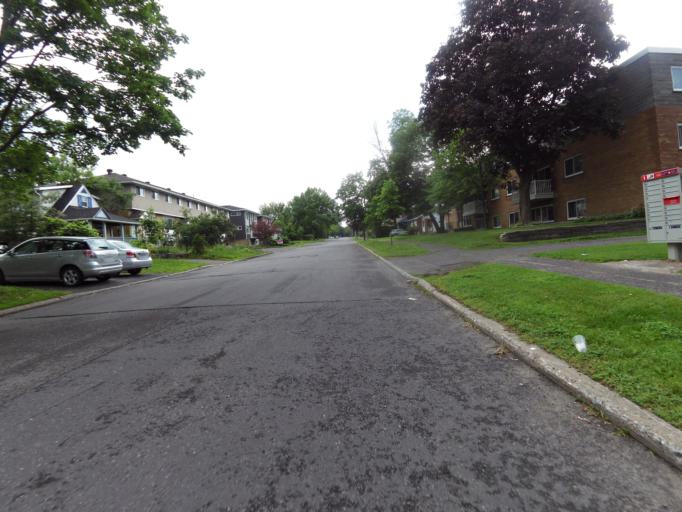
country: CA
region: Ontario
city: Ottawa
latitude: 45.3769
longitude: -75.7294
